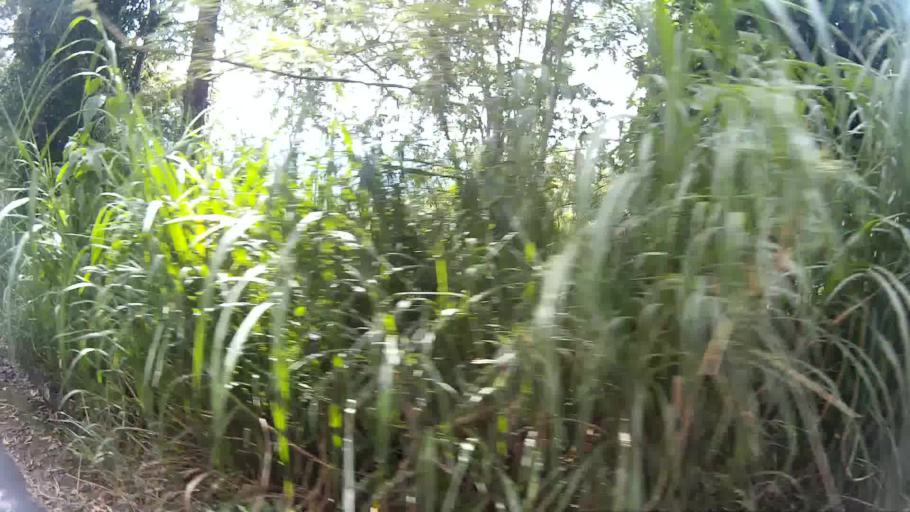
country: CO
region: Caldas
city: Belalcazar
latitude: 4.9489
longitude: -75.8364
